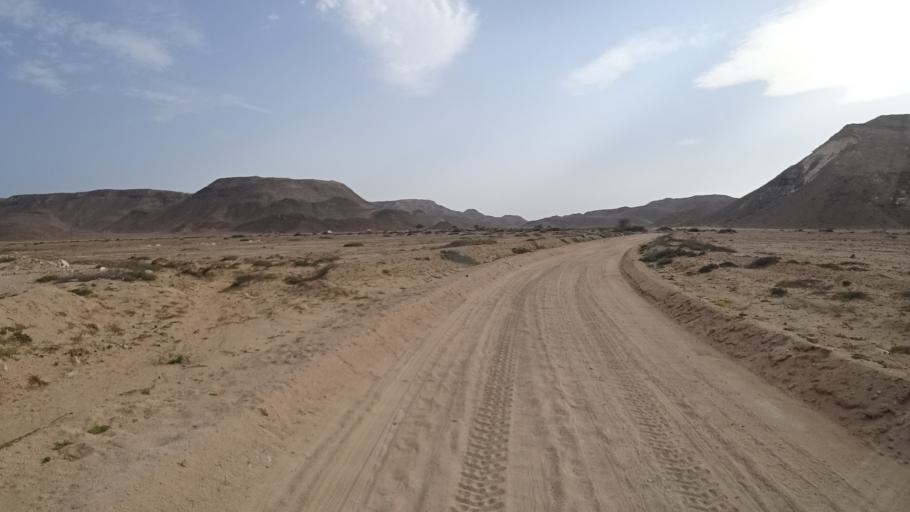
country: OM
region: Ash Sharqiyah
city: Sur
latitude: 22.4380
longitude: 59.8191
